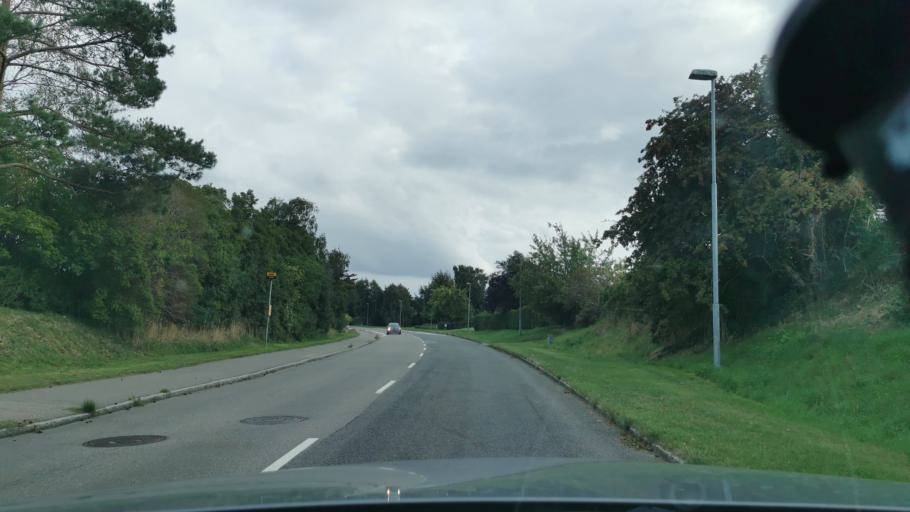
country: DK
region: Zealand
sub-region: Kalundborg Kommune
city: Kalundborg
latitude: 55.6872
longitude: 11.0567
